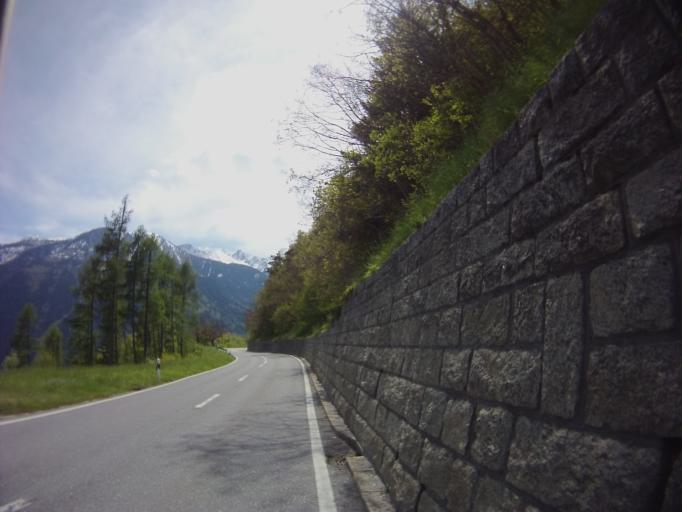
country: CH
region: Valais
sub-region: Martigny District
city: Martigny-Combe
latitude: 46.0899
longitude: 7.0458
